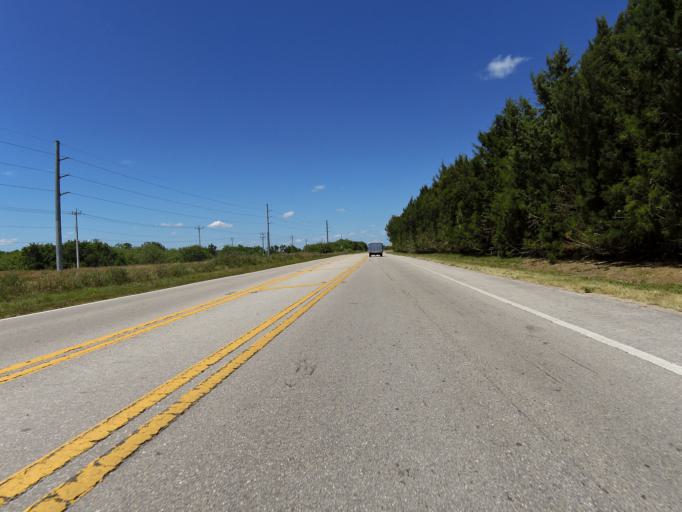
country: US
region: Florida
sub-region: Collier County
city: Immokalee
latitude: 26.3500
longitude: -81.4168
